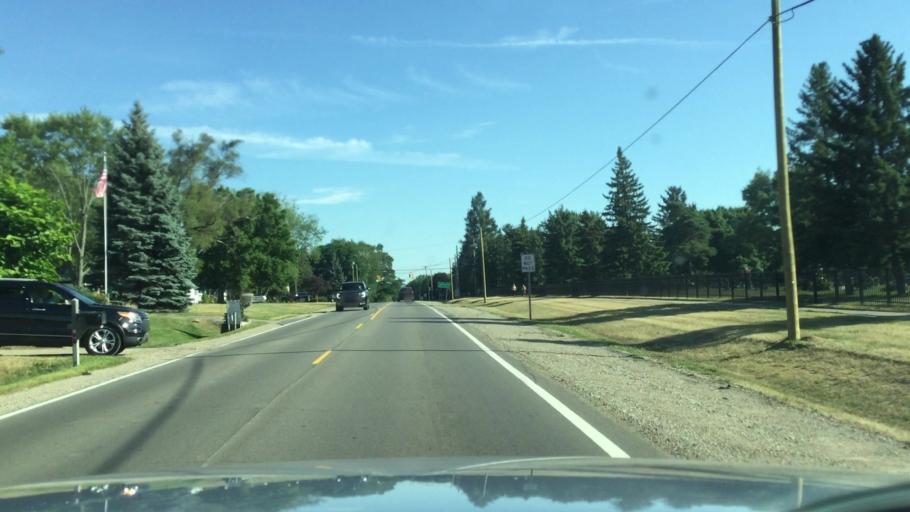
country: US
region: Michigan
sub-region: Oakland County
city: Waterford
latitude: 42.6694
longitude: -83.3867
